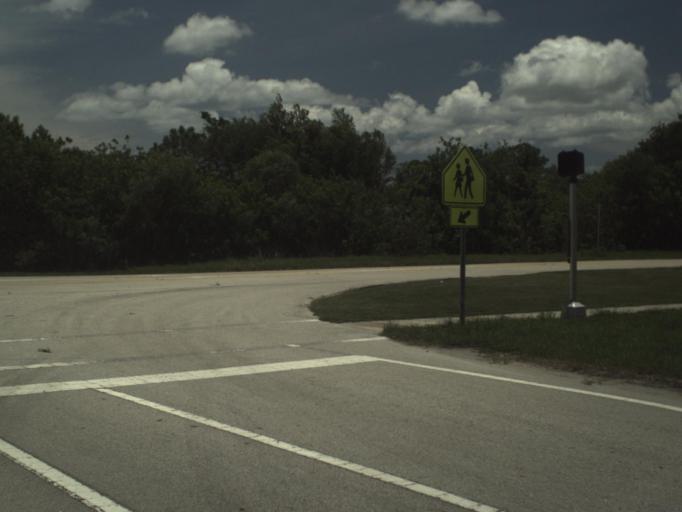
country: US
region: Florida
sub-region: Martin County
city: Port Salerno
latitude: 27.1213
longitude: -80.2391
